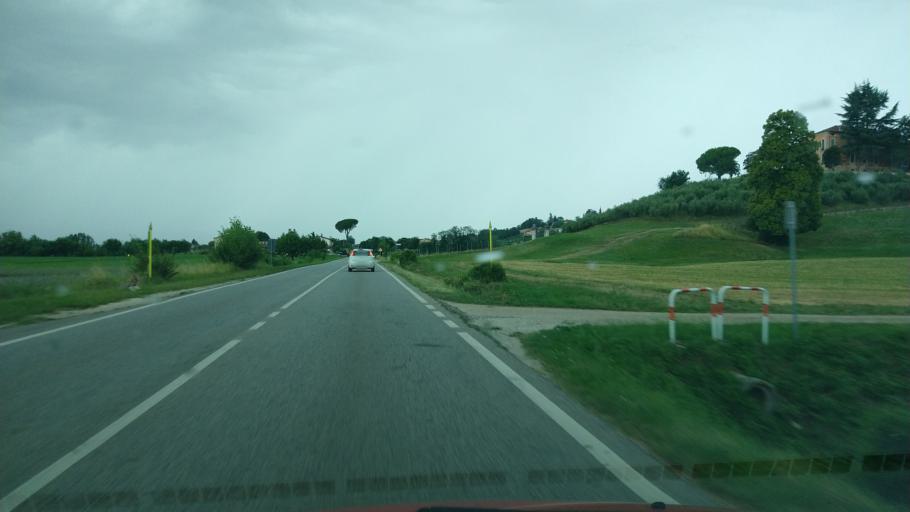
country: IT
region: Veneto
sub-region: Provincia di Vicenza
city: Grumolo Pedemonte
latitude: 45.7298
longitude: 11.5057
